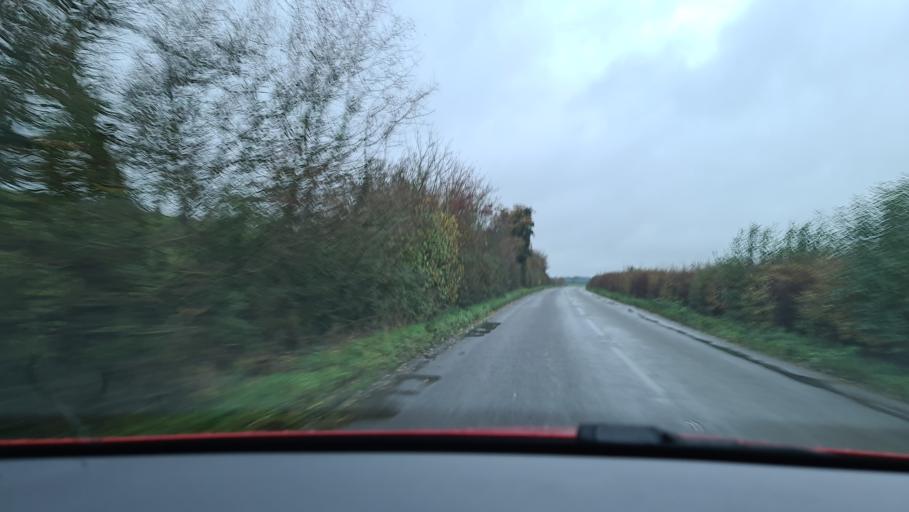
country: GB
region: England
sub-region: Oxfordshire
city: Somerton
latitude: 51.9265
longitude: -1.2215
